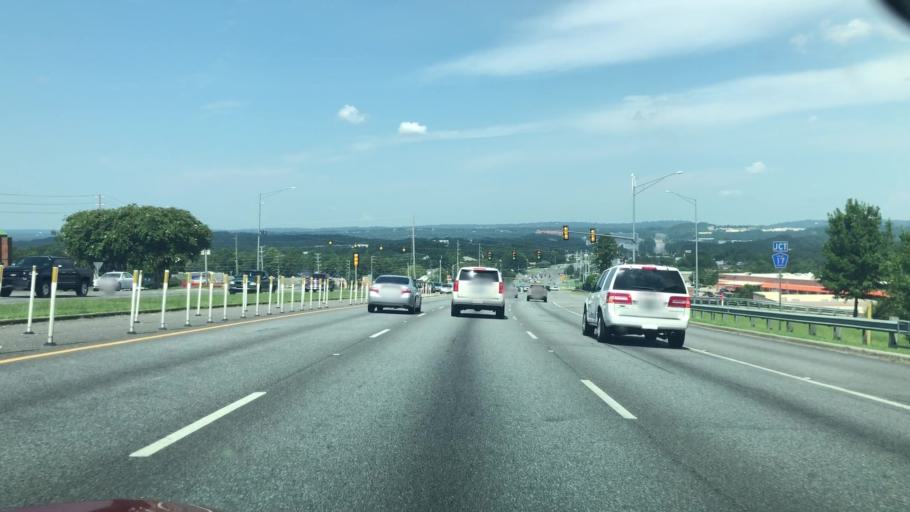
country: US
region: Alabama
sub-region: Shelby County
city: Lake Purdy
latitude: 33.4188
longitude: -86.6914
